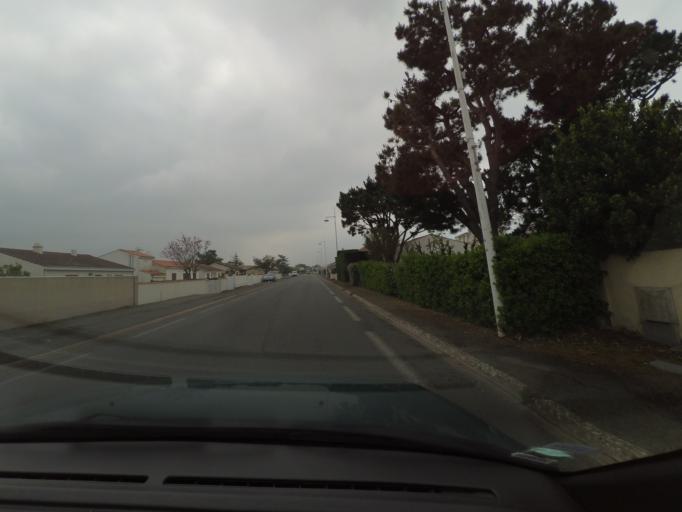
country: FR
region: Pays de la Loire
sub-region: Departement de la Vendee
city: Angles
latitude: 46.3375
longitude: -1.3355
